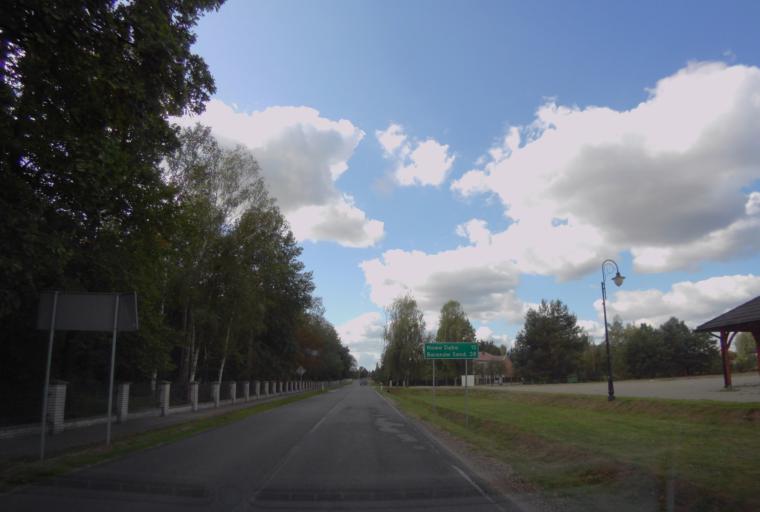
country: PL
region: Subcarpathian Voivodeship
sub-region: Powiat stalowowolski
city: Bojanow
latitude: 50.4252
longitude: 21.9510
